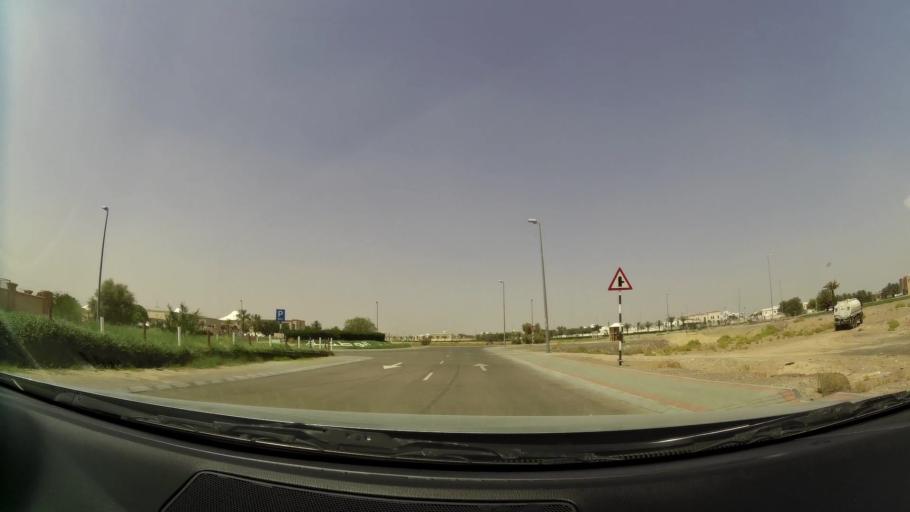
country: AE
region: Abu Dhabi
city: Al Ain
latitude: 24.2565
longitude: 55.6911
